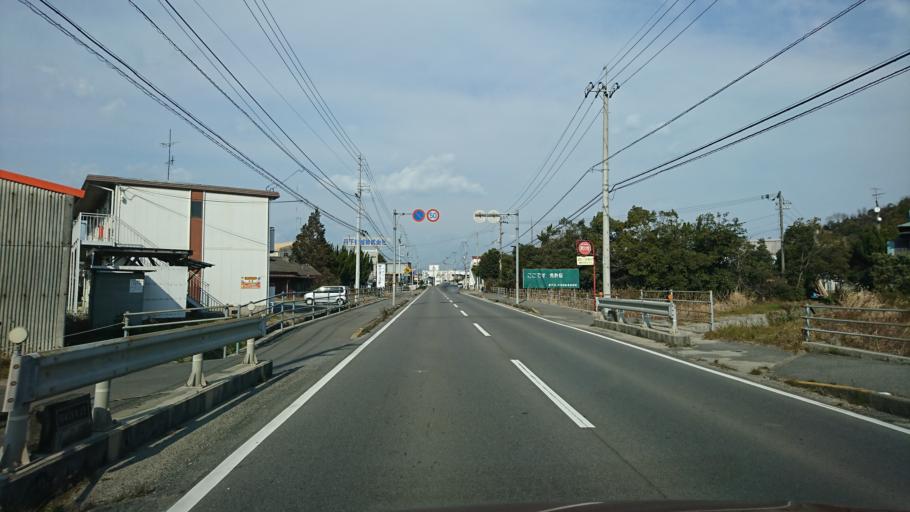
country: JP
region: Ehime
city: Saijo
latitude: 34.0104
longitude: 133.0386
